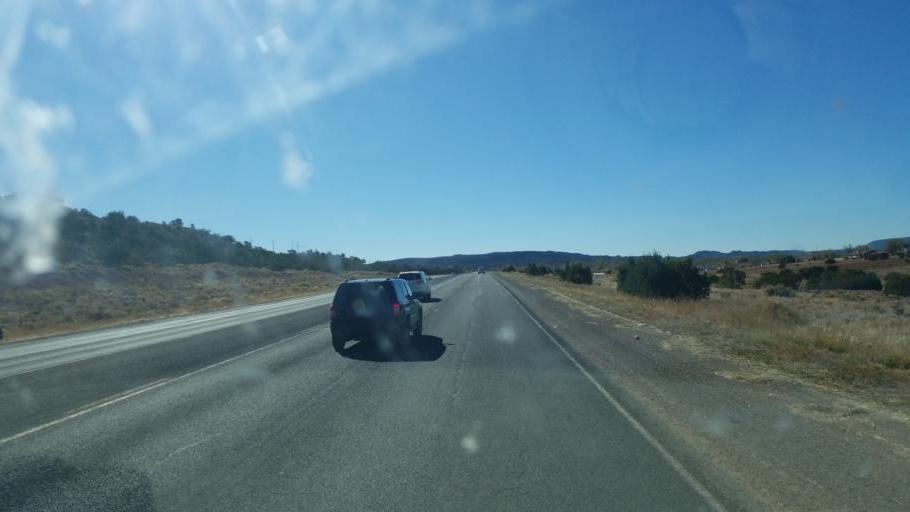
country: US
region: Arizona
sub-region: Apache County
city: Window Rock
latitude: 35.6848
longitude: -109.0634
